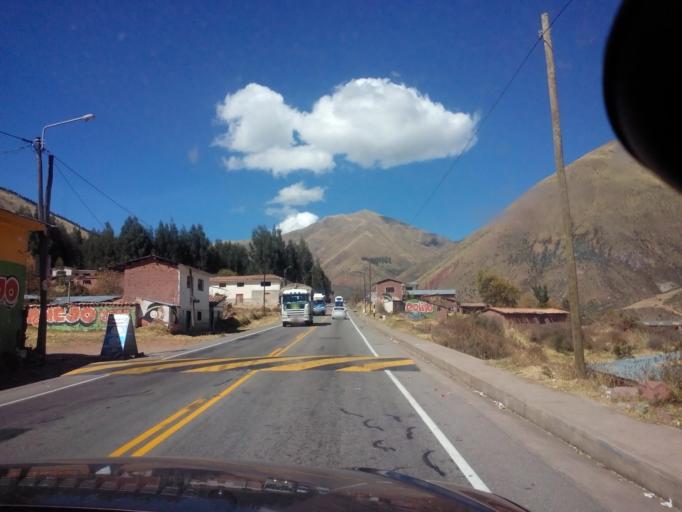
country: PE
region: Cusco
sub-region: Provincia de Quispicanchis
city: Cusipata
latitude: -13.9627
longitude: -71.4956
